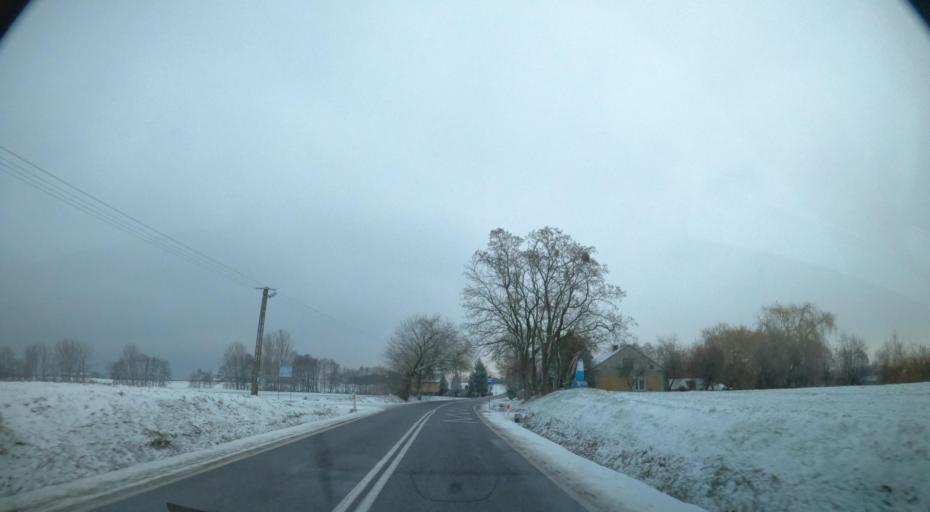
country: PL
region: Masovian Voivodeship
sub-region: Powiat plocki
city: Nowy Duninow
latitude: 52.6289
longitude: 19.4244
